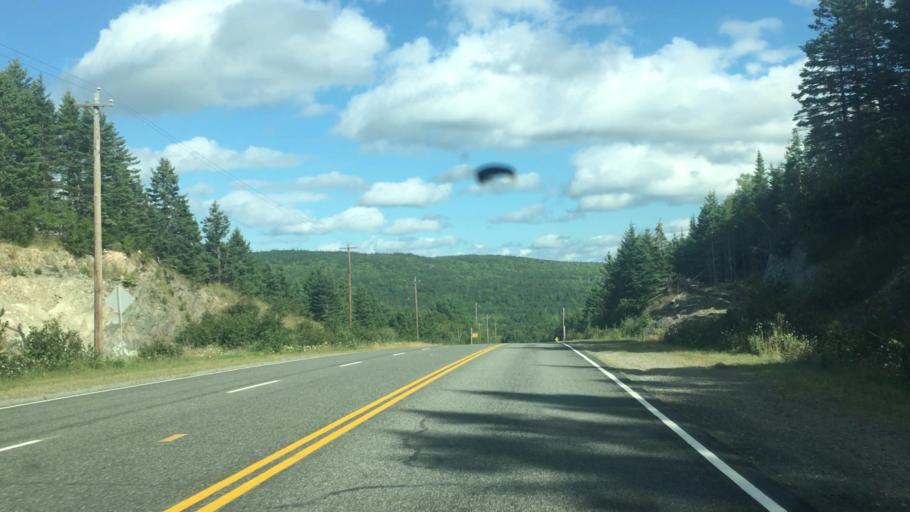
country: CA
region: Nova Scotia
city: Sydney
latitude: 45.8143
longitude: -60.6826
